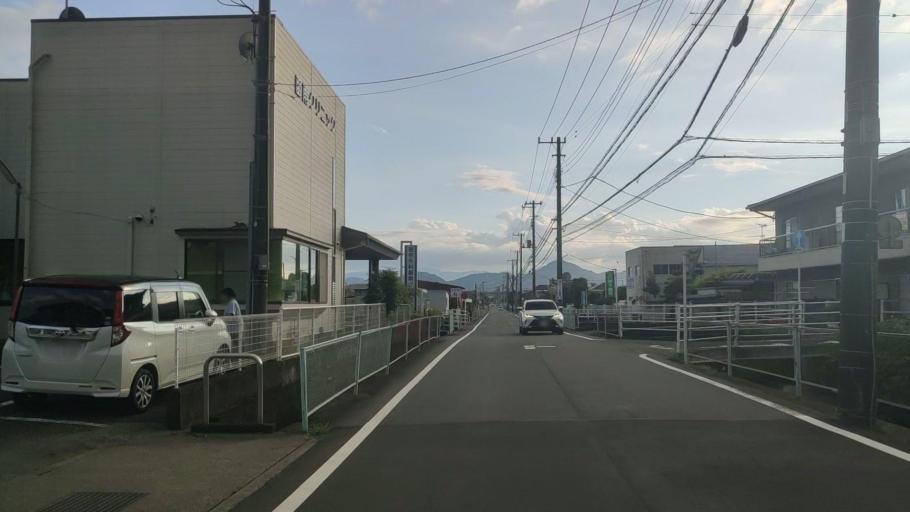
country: JP
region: Shizuoka
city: Mishima
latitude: 35.0959
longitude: 138.9516
